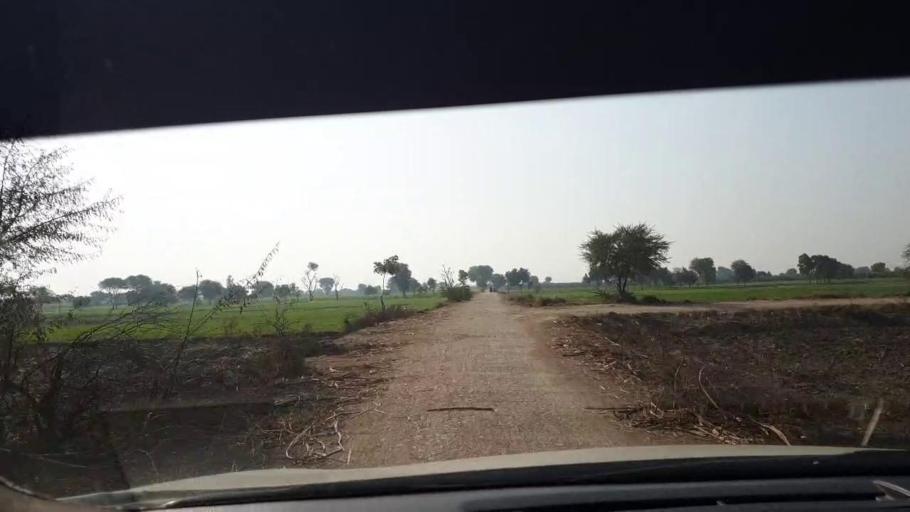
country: PK
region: Sindh
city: Tando Adam
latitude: 25.7654
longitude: 68.7246
